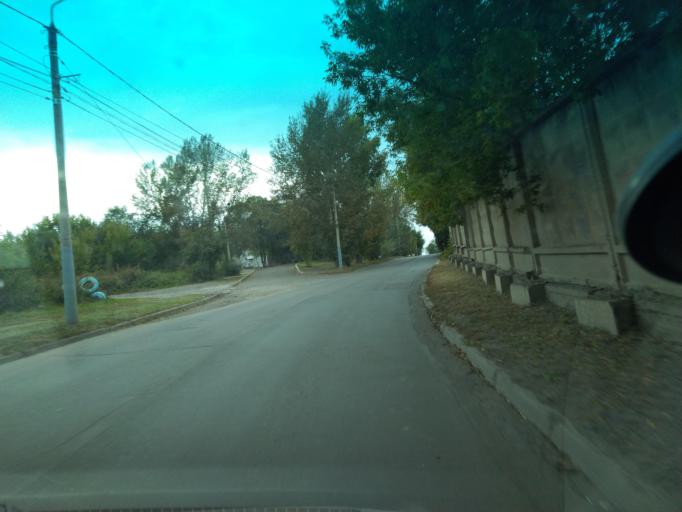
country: RU
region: Krasnoyarskiy
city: Berezovka
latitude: 55.9864
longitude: 93.0086
